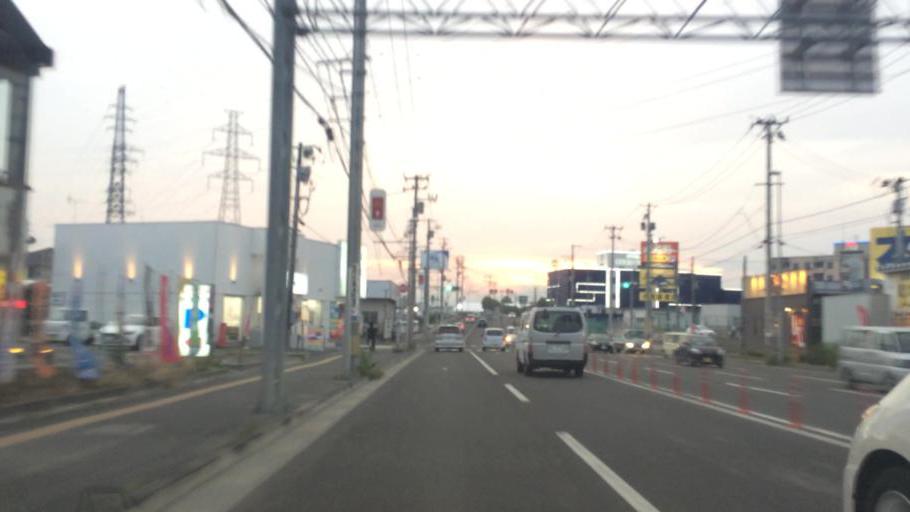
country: JP
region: Miyagi
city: Sendai-shi
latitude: 38.3157
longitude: 140.8993
